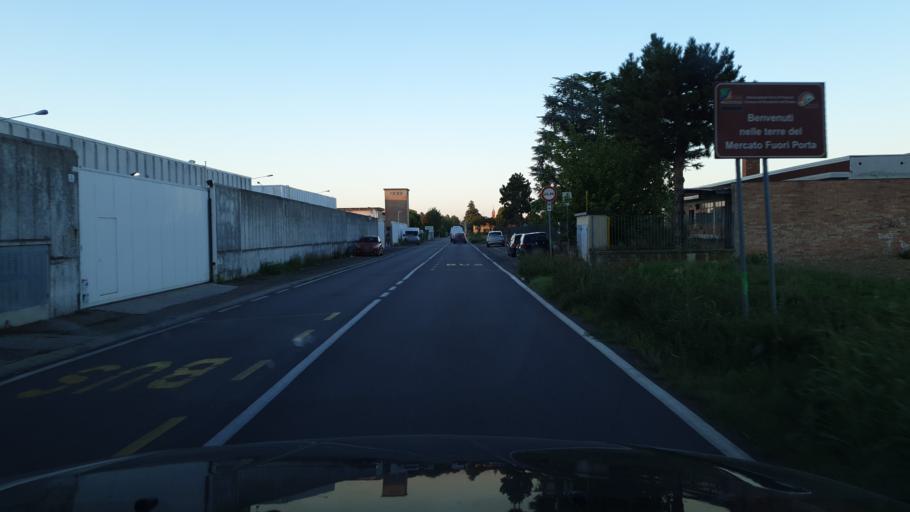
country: IT
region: Emilia-Romagna
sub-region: Provincia di Bologna
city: Quarto Inferiore
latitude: 44.5428
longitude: 11.3952
